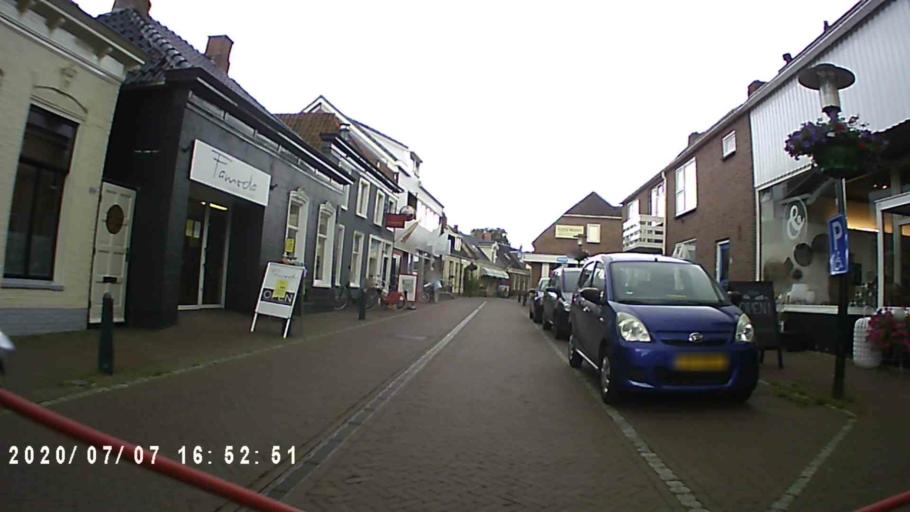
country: NL
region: Groningen
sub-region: Gemeente Winsum
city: Winsum
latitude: 53.3334
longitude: 6.5148
